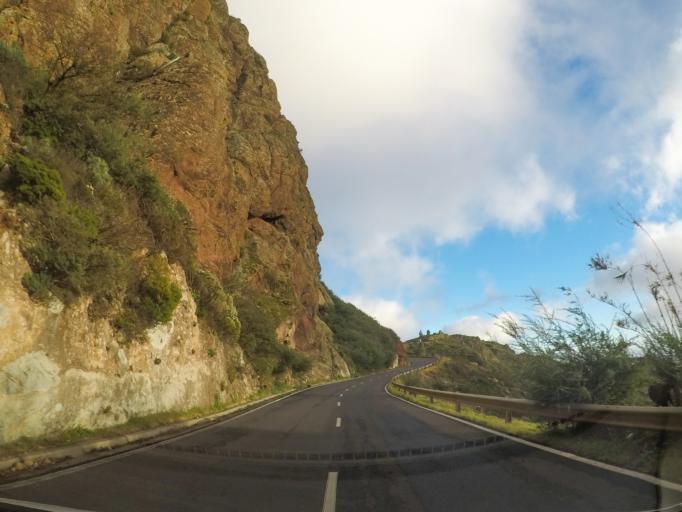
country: ES
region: Canary Islands
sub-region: Provincia de Santa Cruz de Tenerife
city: Alajero
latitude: 28.0889
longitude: -17.2517
